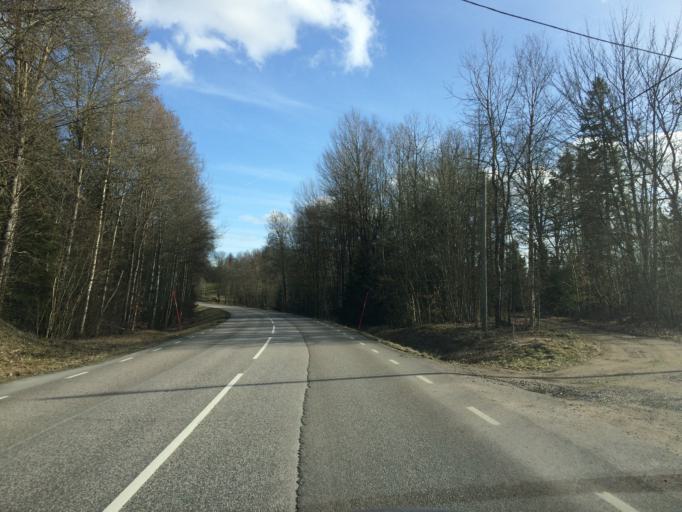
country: SE
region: Kronoberg
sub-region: Almhults Kommun
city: AElmhult
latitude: 56.6313
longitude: 14.0320
